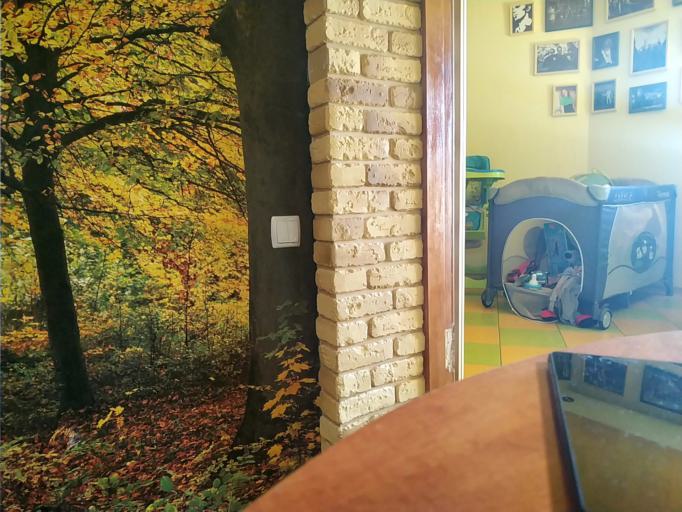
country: RU
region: Tverskaya
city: Vyshniy Volochek
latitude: 57.6061
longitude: 34.5002
